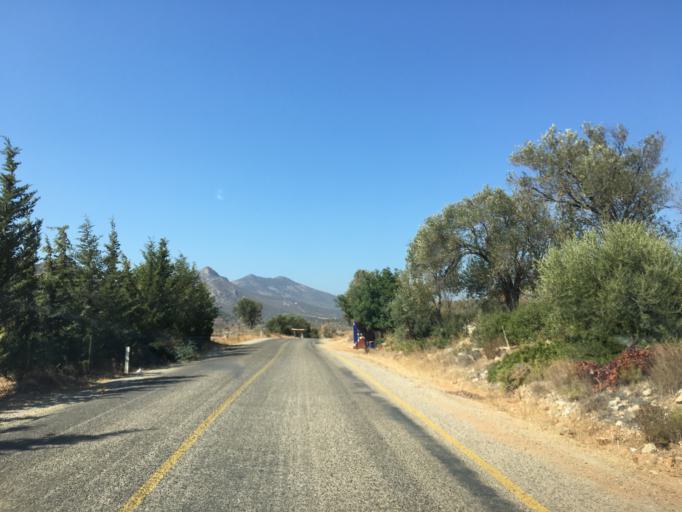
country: TR
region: Mugla
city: Datca
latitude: 36.6946
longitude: 27.4715
